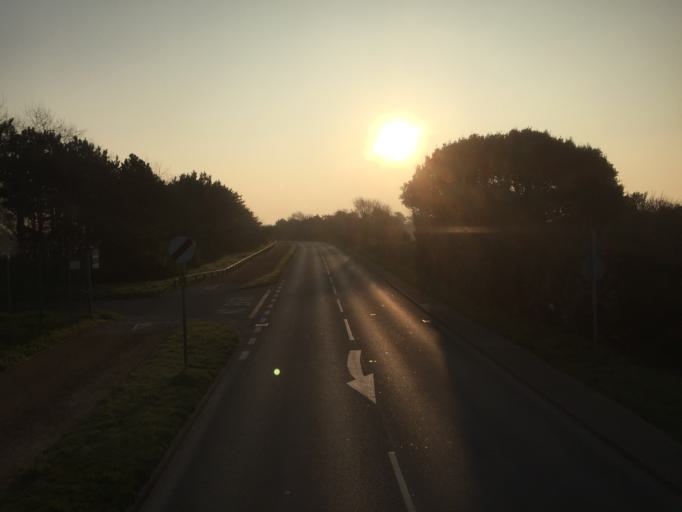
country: JE
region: St Helier
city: Saint Helier
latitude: 49.2024
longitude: -2.1938
